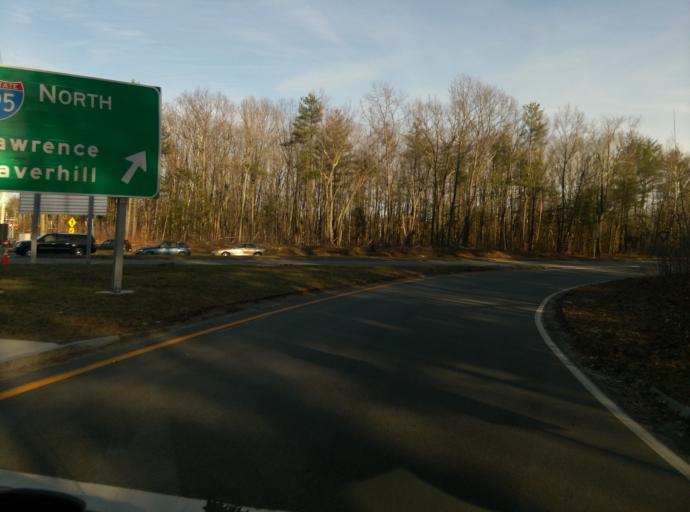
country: US
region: Massachusetts
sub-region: Middlesex County
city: Tewksbury
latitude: 42.6427
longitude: -71.2302
